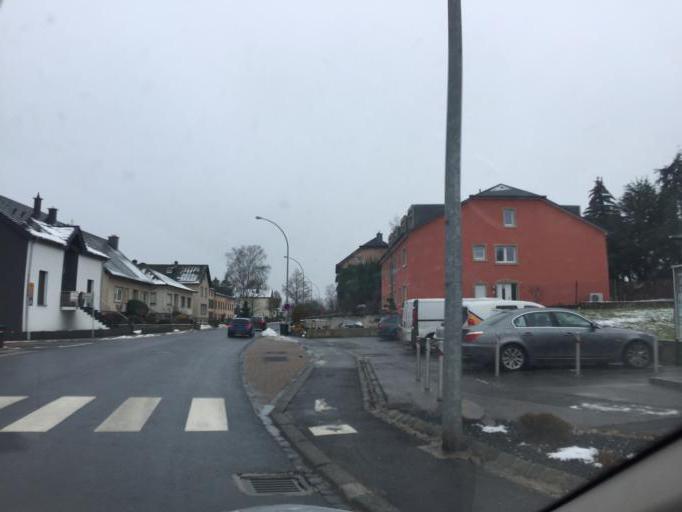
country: LU
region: Diekirch
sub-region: Canton de Diekirch
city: Niederfeulen
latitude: 49.8544
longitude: 6.0442
